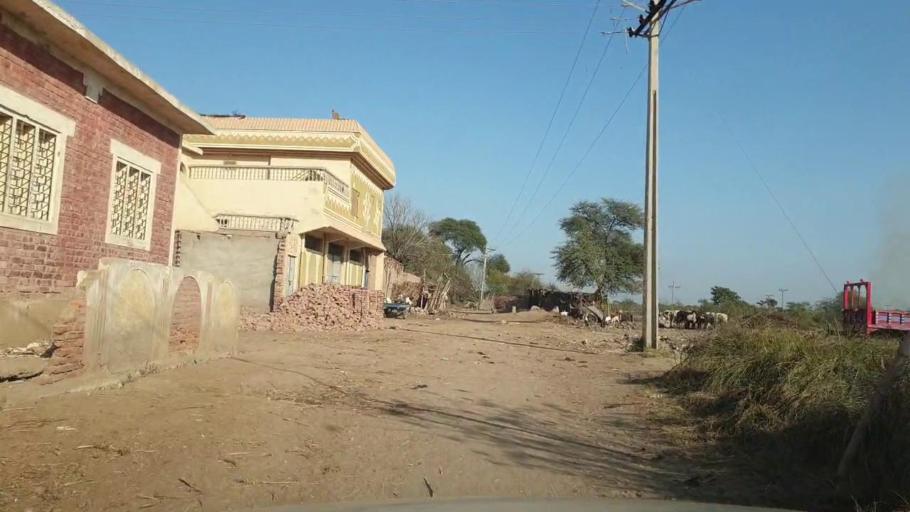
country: PK
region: Sindh
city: Tando Allahyar
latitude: 25.5152
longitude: 68.6565
